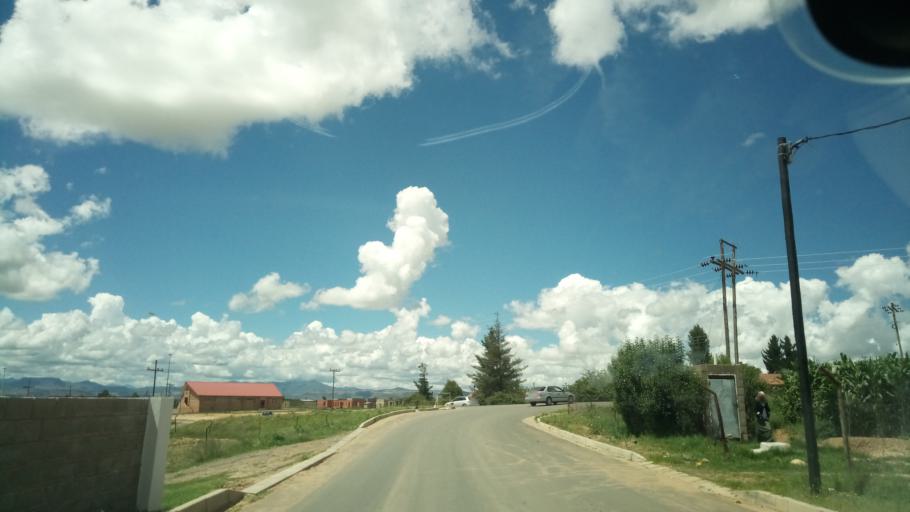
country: LS
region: Maseru
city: Maseru
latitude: -29.3692
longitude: 27.5396
